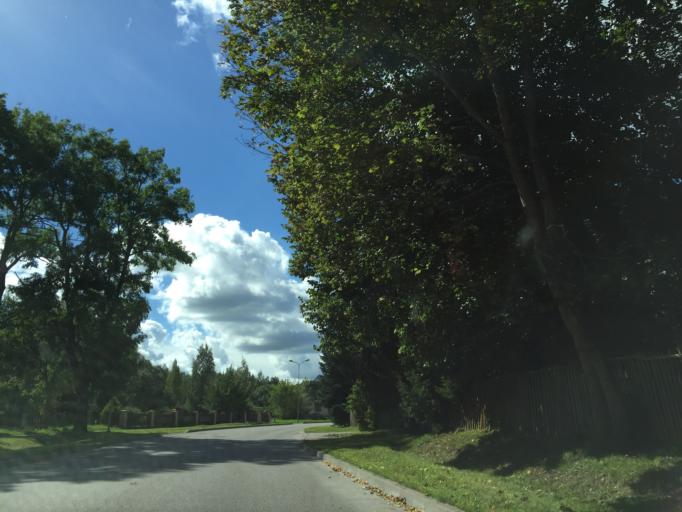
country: LV
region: Kuldigas Rajons
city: Kuldiga
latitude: 56.9666
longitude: 21.9478
